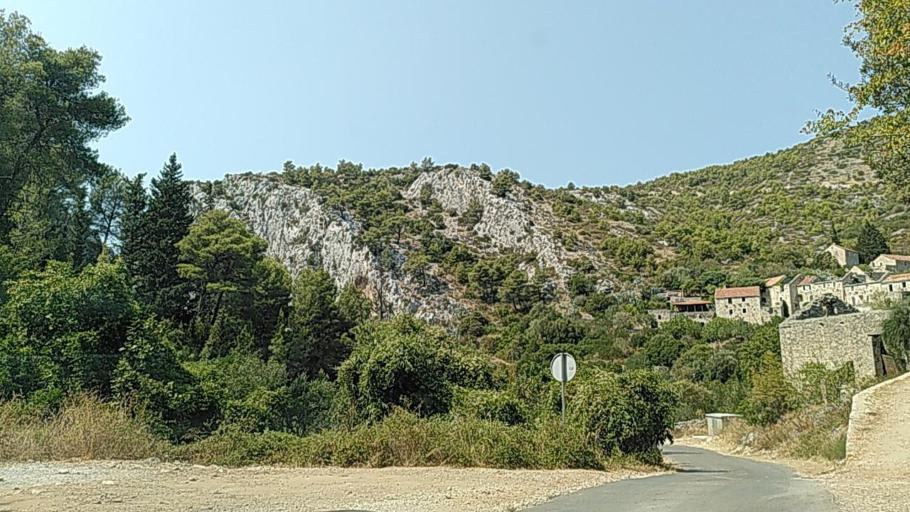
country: HR
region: Splitsko-Dalmatinska
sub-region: Grad Hvar
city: Hvar
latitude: 43.1674
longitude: 16.5036
